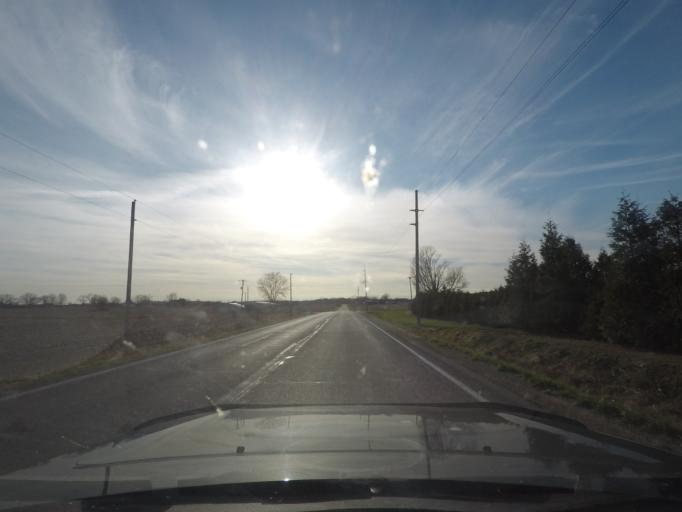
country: US
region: Indiana
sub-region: Saint Joseph County
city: Walkerton
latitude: 41.4481
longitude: -86.4240
